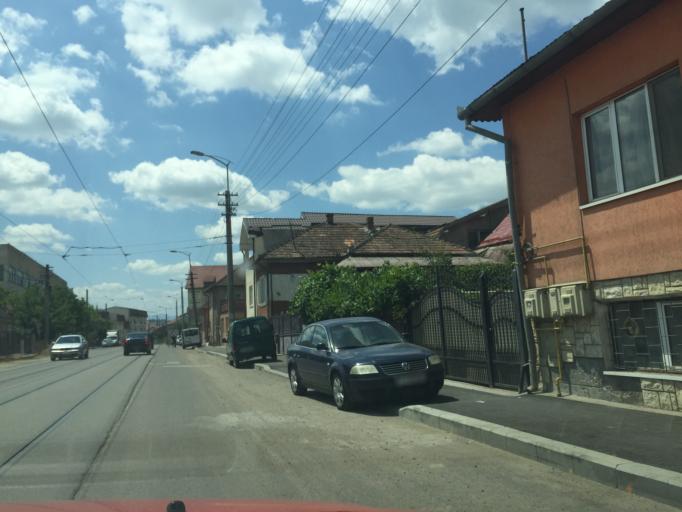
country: RO
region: Cluj
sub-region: Municipiul Cluj-Napoca
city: Cluj-Napoca
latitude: 46.7971
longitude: 23.6047
